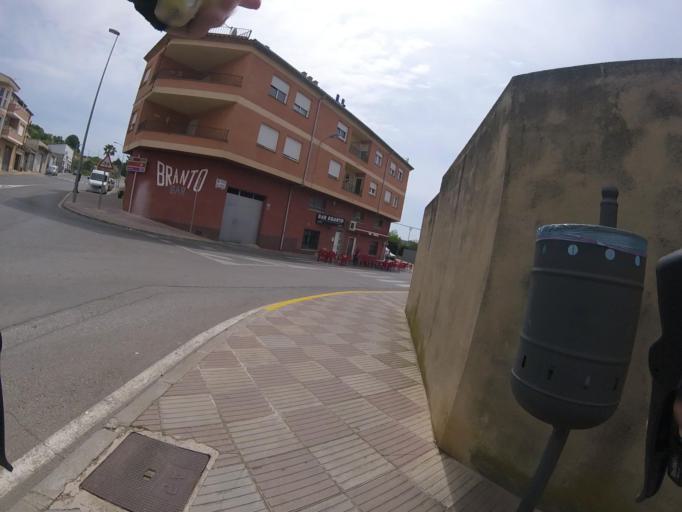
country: ES
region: Valencia
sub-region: Provincia de Castello
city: Cabanes
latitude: 40.1545
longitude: 0.0476
